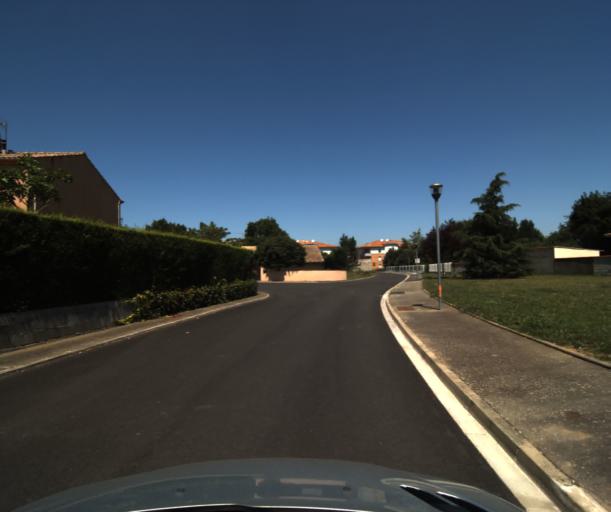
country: FR
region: Midi-Pyrenees
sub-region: Departement de la Haute-Garonne
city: Roquettes
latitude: 43.4961
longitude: 1.3670
